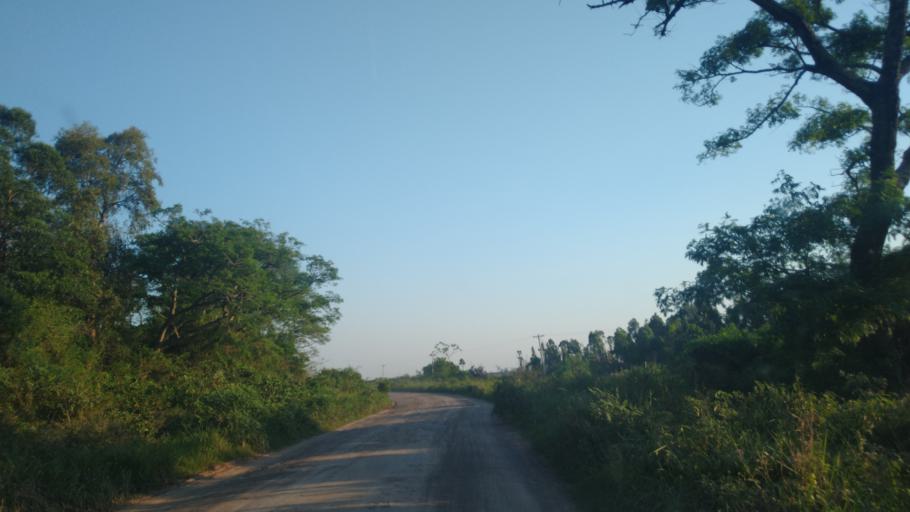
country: PY
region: Neembucu
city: Cerrito
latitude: -27.3966
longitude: -57.6584
